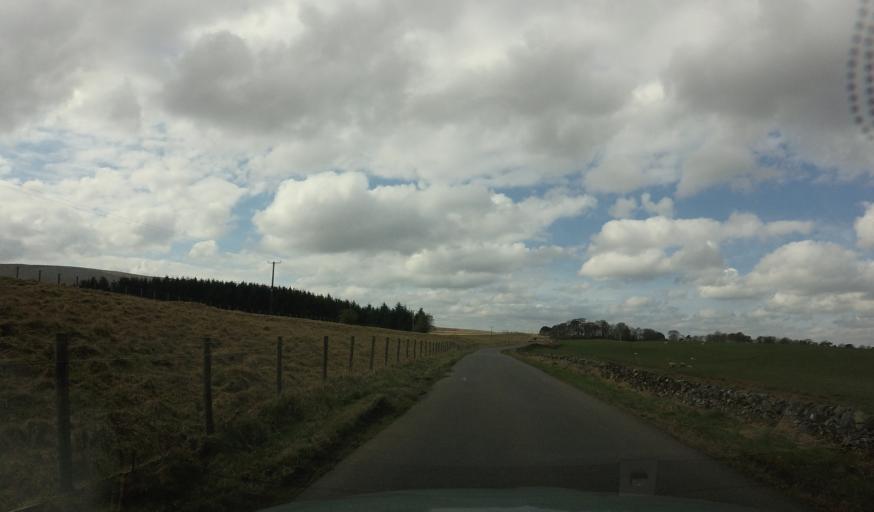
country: GB
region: Scotland
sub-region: Midlothian
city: Penicuik
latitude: 55.7657
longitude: -3.1427
